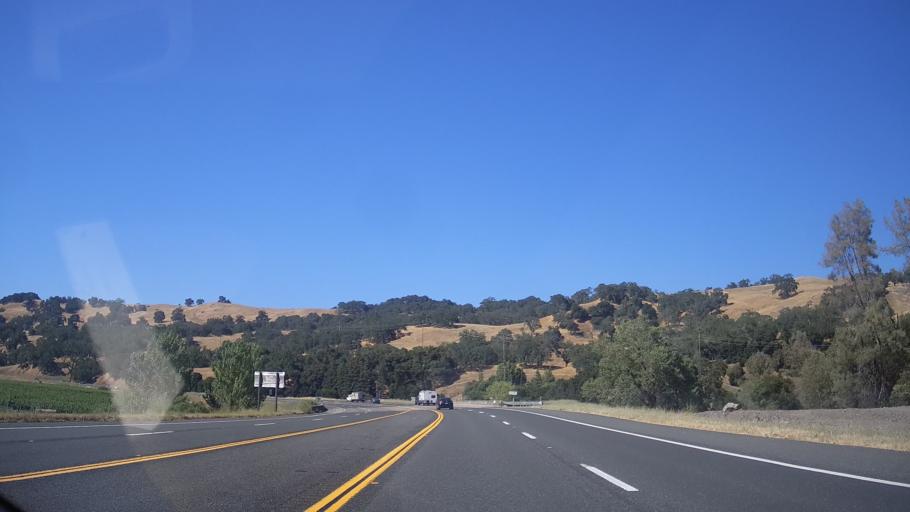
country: US
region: California
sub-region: Sonoma County
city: Cloverdale
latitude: 38.9240
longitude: -123.0568
